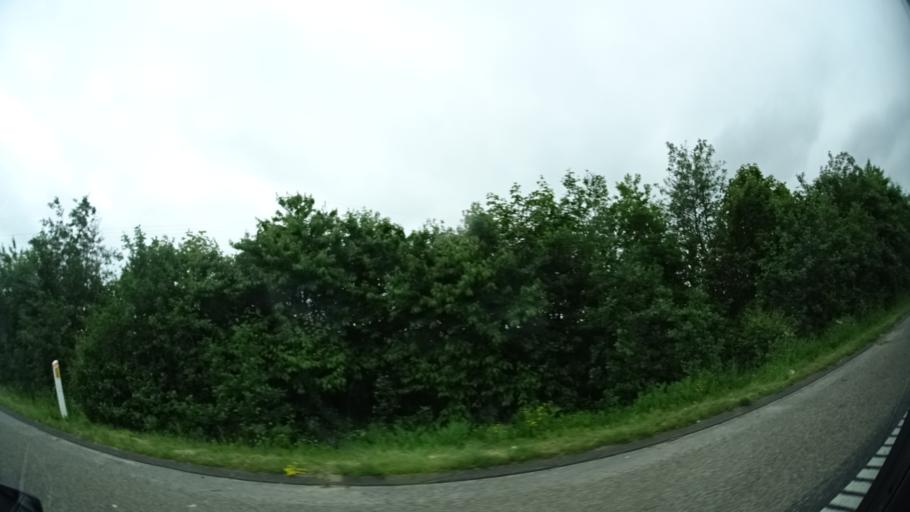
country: DK
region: Central Jutland
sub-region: Skanderborg Kommune
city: Horning
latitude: 56.1128
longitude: 10.0393
